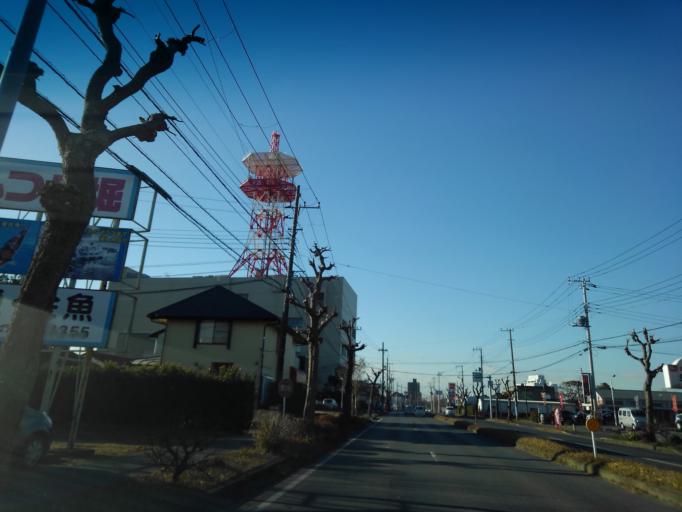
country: JP
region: Chiba
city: Kimitsu
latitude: 35.3259
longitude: 139.9082
